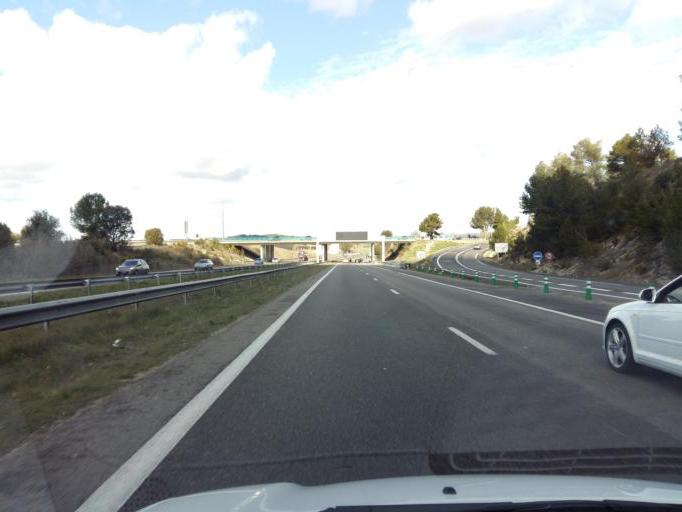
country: FR
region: Provence-Alpes-Cote d'Azur
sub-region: Departement des Bouches-du-Rhone
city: Bouc-Bel-Air
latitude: 43.4698
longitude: 5.4073
